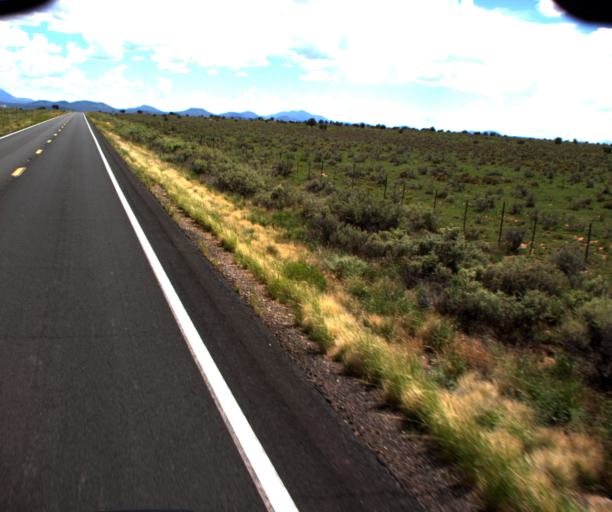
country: US
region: Arizona
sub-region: Coconino County
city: Williams
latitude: 35.6337
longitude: -112.1205
